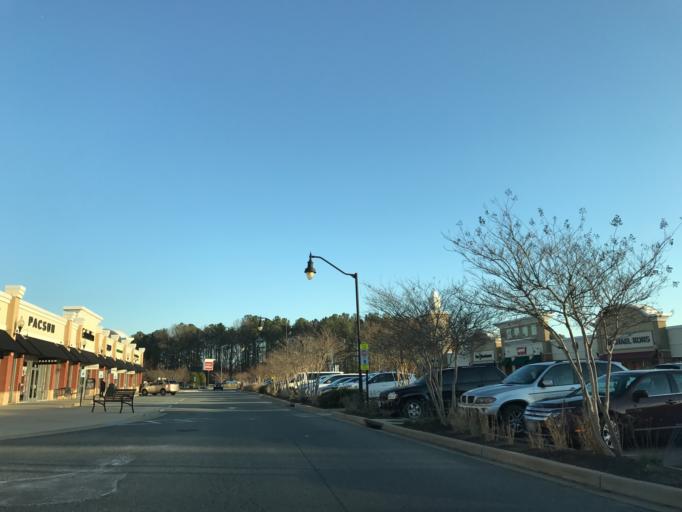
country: US
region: Maryland
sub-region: Queen Anne's County
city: Grasonville
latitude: 38.9833
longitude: -76.1607
